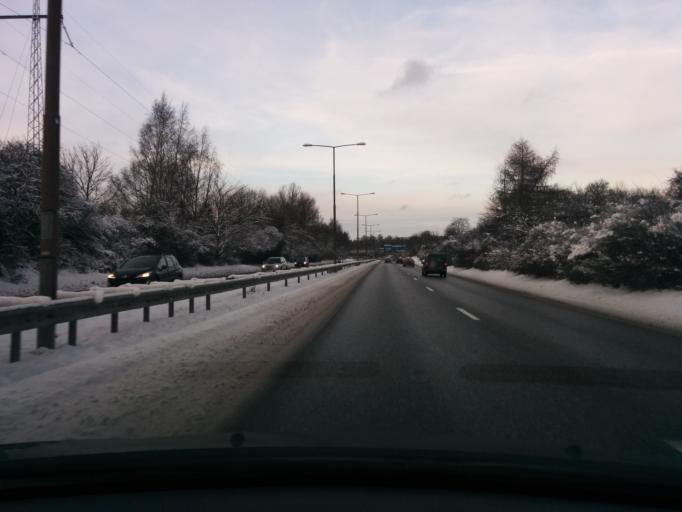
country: SE
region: Stockholm
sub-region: Stockholms Kommun
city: Arsta
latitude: 59.2770
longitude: 18.0401
